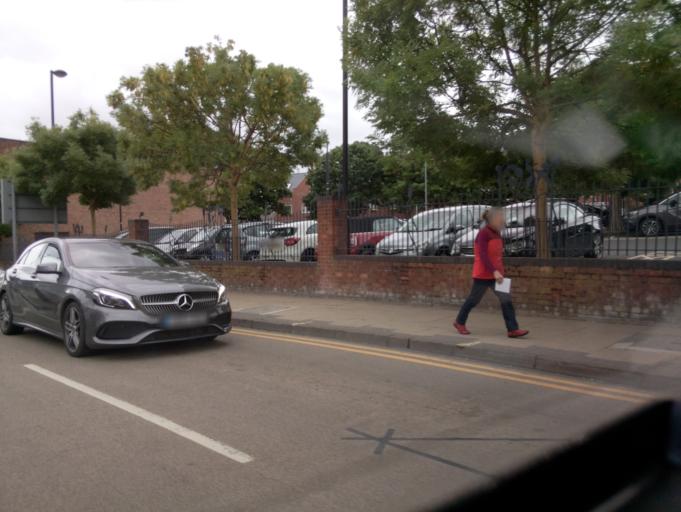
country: GB
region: England
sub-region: Worcestershire
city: Worcester
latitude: 52.1881
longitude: -2.2181
